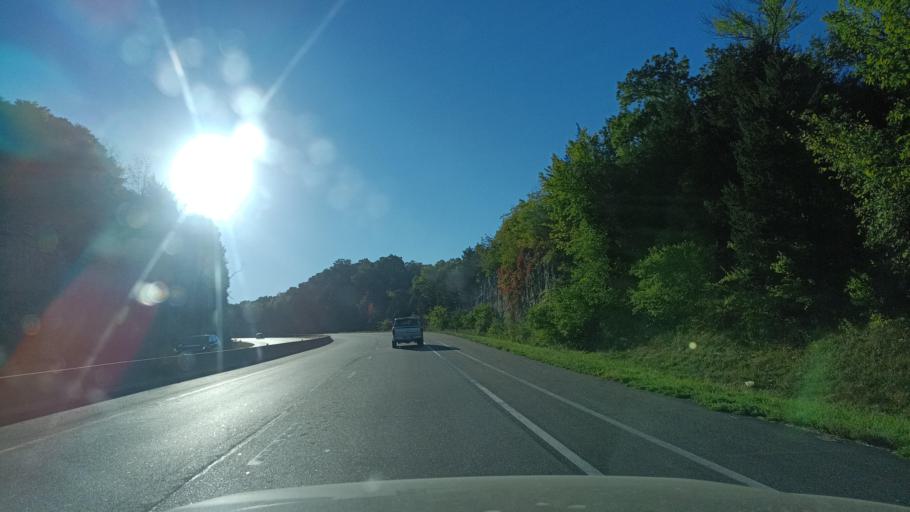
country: US
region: Missouri
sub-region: Boone County
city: Columbia
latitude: 38.9313
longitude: -92.3103
